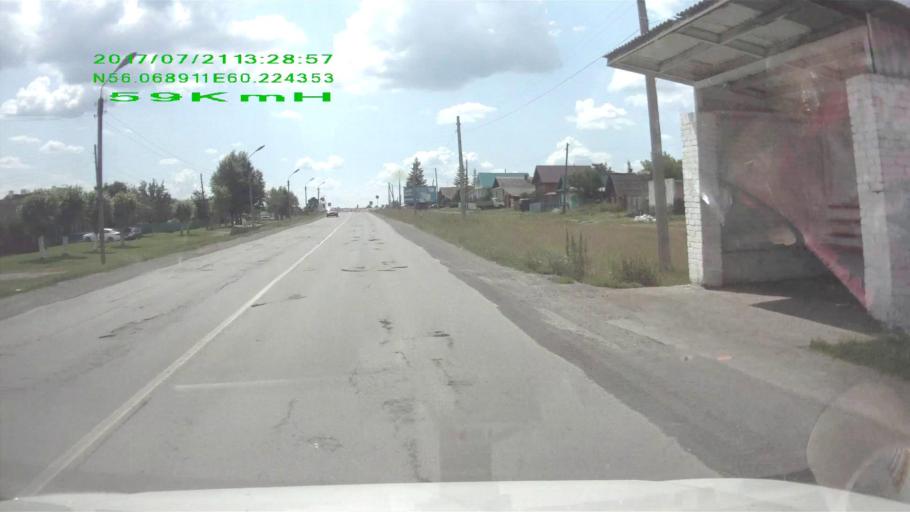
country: RU
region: Chelyabinsk
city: Verkhniy Ufaley
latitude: 56.0682
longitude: 60.2235
